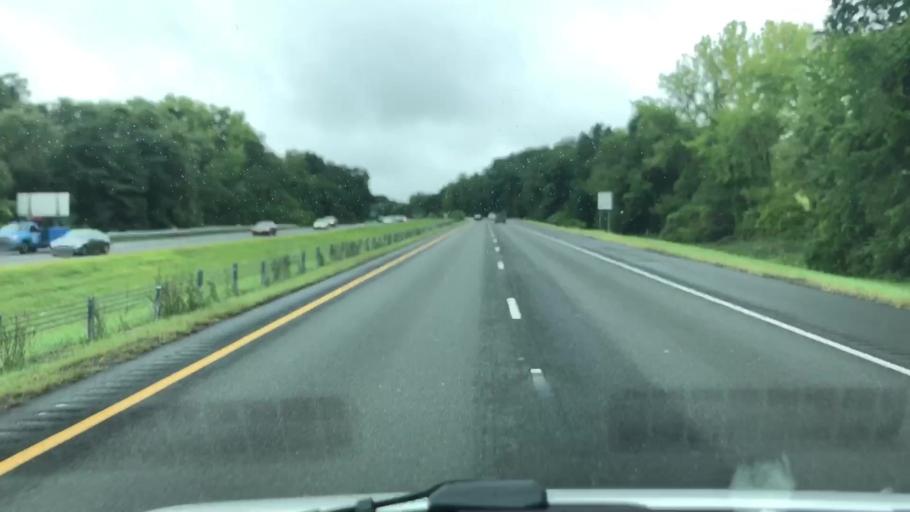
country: US
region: Massachusetts
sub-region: Hampden County
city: Holyoke
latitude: 42.2324
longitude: -72.6348
